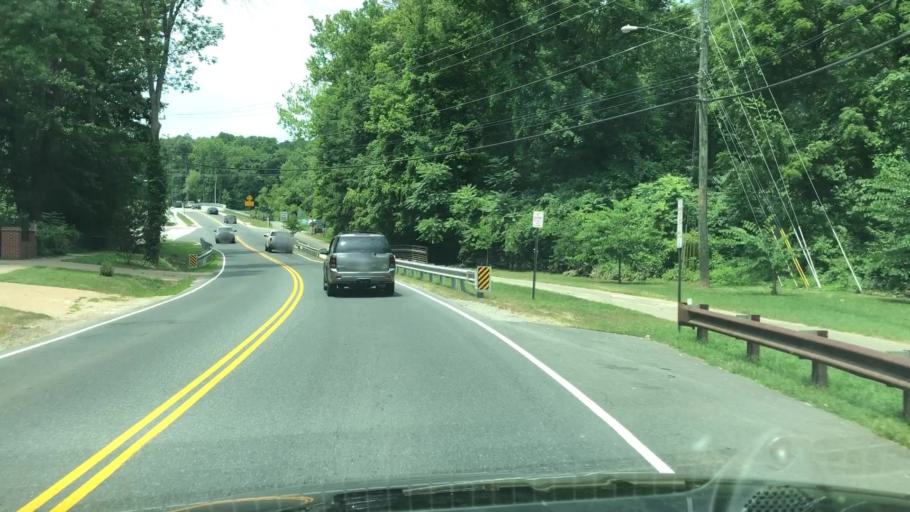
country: US
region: Virginia
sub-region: Stafford County
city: Falmouth
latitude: 38.3166
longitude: -77.4836
